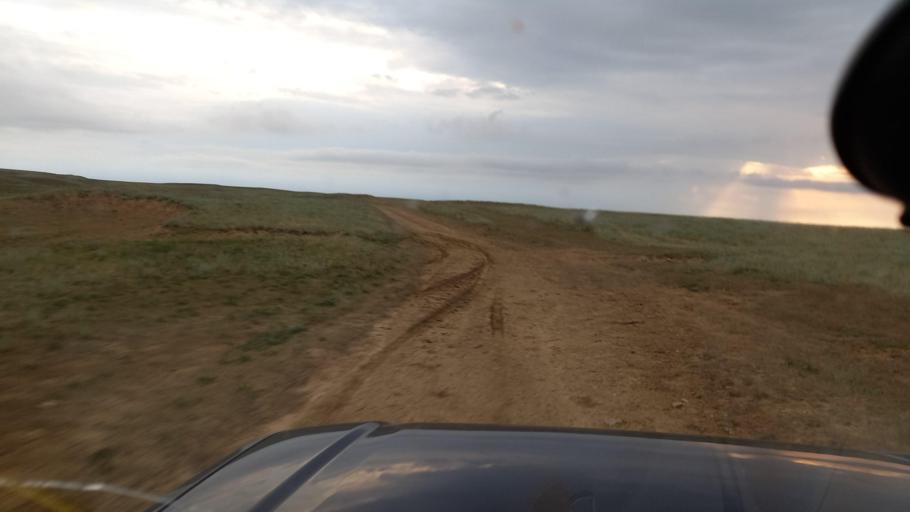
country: RU
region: Krasnodarskiy
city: Taman'
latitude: 45.2071
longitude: 36.7893
